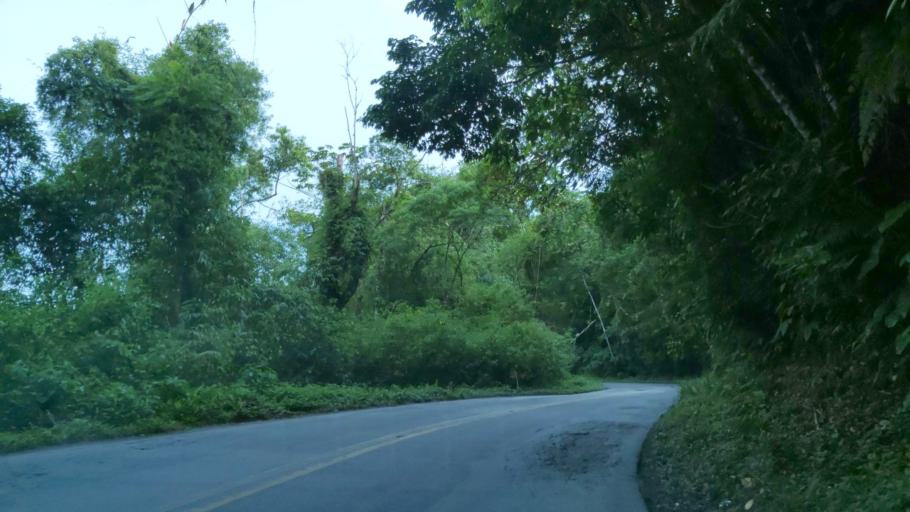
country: BR
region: Sao Paulo
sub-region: Miracatu
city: Miracatu
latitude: -24.0443
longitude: -47.5683
